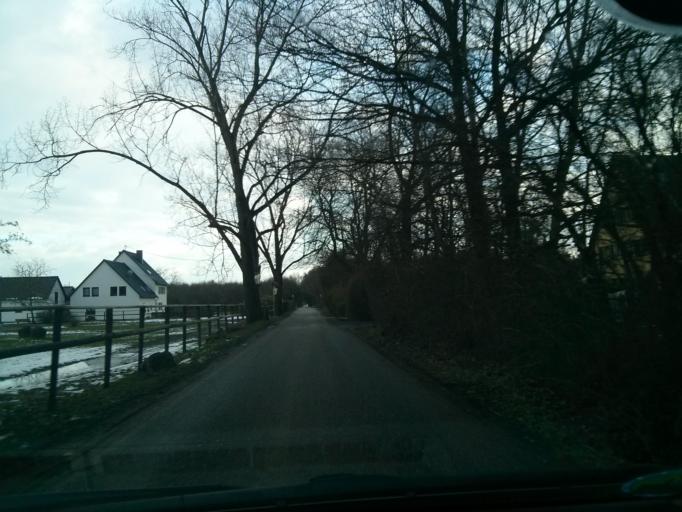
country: DE
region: North Rhine-Westphalia
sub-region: Regierungsbezirk Koln
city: Alfter
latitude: 50.6859
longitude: 6.9968
